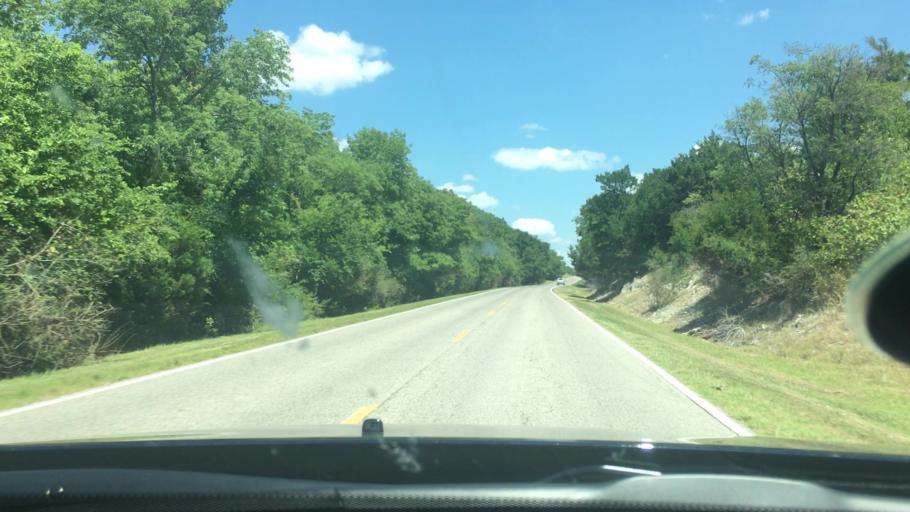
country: US
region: Oklahoma
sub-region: Carter County
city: Dickson
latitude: 34.3123
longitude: -96.9624
